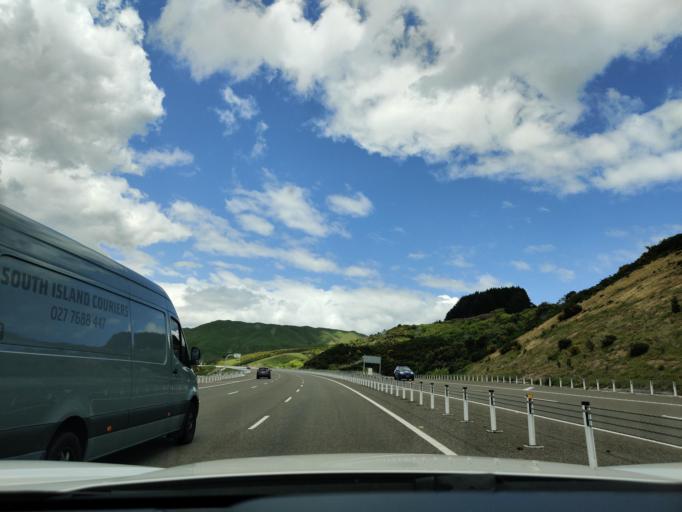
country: NZ
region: Wellington
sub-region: Porirua City
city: Porirua
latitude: -41.1529
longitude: 174.8594
